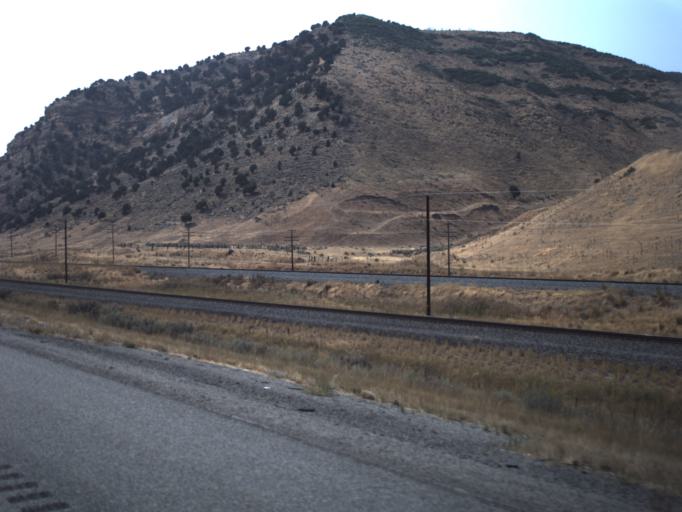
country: US
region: Utah
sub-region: Summit County
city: Coalville
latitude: 41.0724
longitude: -111.2609
